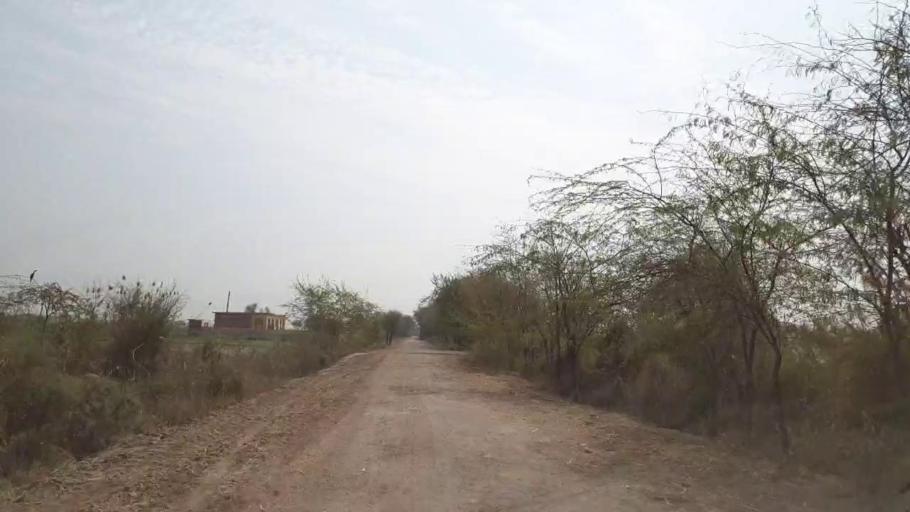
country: PK
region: Sindh
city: Mirpur Khas
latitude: 25.5553
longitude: 69.0905
